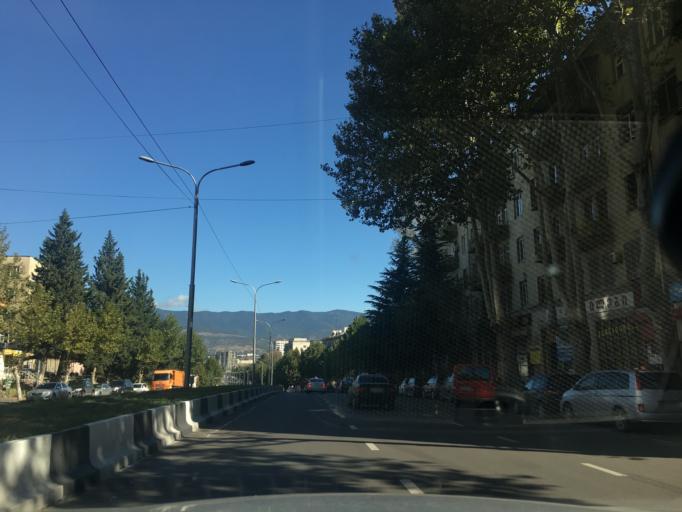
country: GE
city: Zahesi
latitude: 41.7727
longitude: 44.7941
